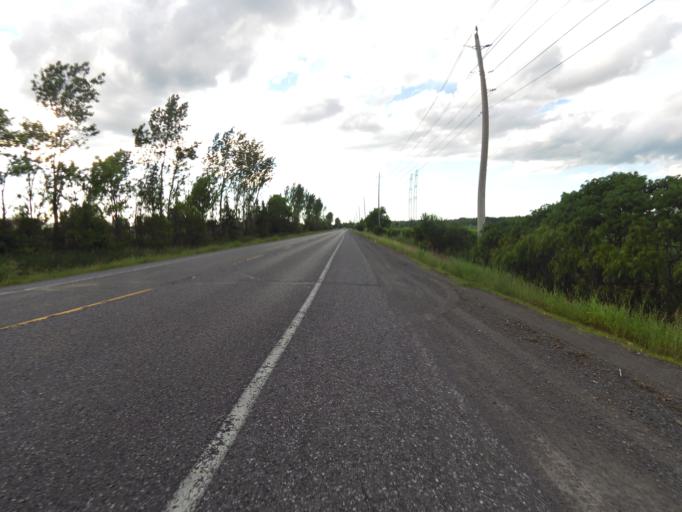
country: CA
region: Ontario
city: Bells Corners
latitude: 45.3060
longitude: -75.7950
